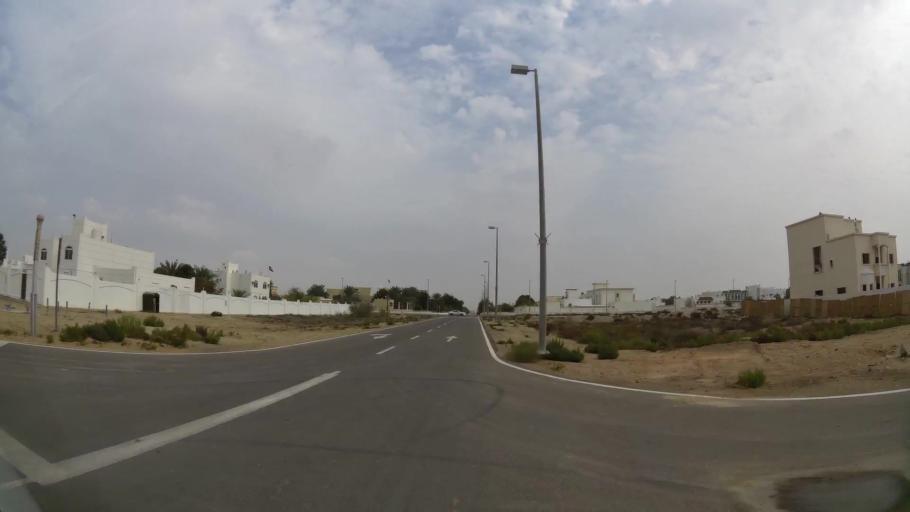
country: AE
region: Abu Dhabi
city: Abu Dhabi
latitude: 24.6358
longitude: 54.7194
